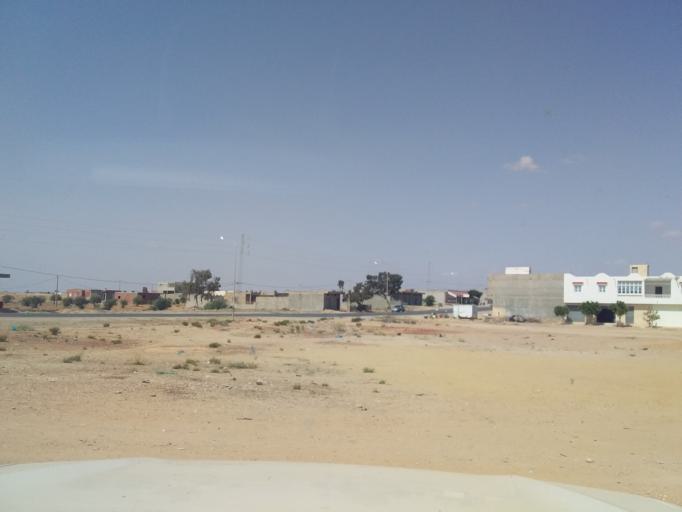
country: TN
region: Madanin
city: Medenine
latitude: 33.6049
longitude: 10.3035
